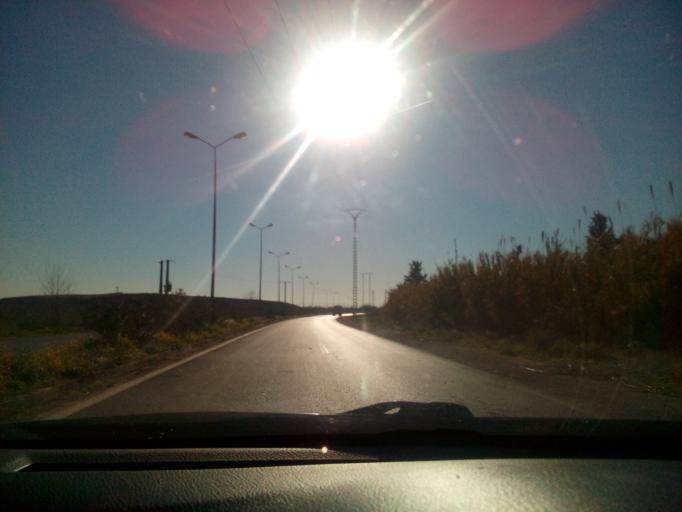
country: DZ
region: Relizane
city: Relizane
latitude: 35.7424
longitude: 0.6074
